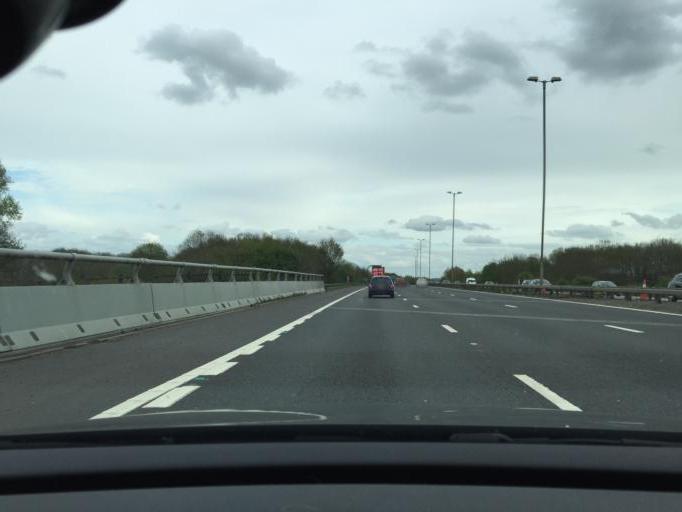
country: GB
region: England
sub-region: West Berkshire
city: Calcot
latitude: 51.4357
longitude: -1.0573
